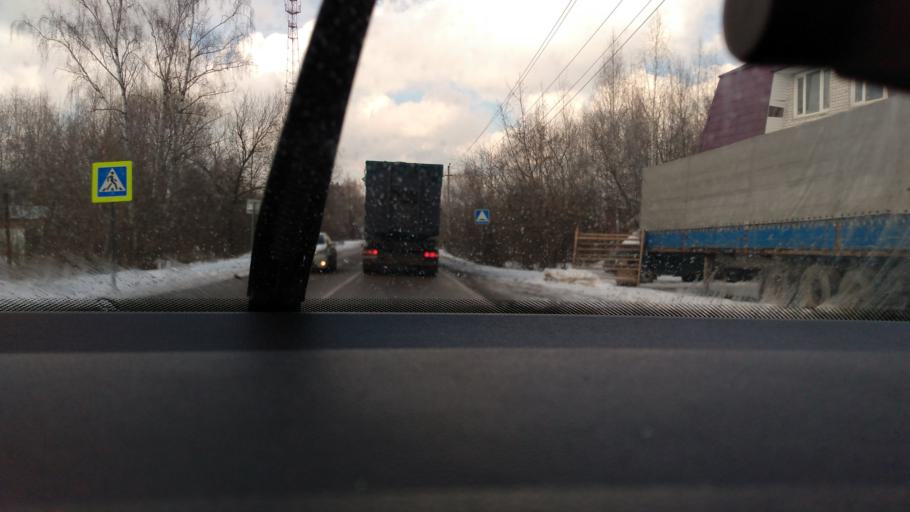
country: RU
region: Moskovskaya
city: Rodniki
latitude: 55.6900
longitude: 38.0790
